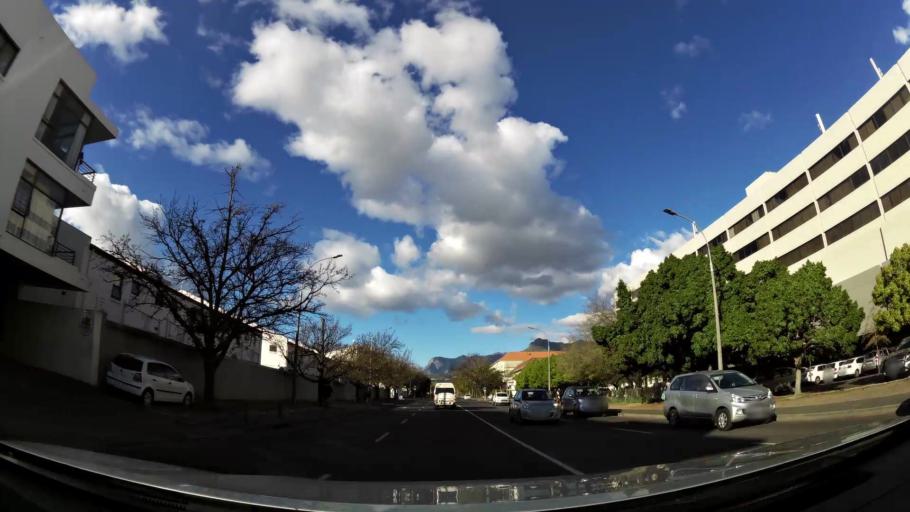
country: ZA
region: Western Cape
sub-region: Cape Winelands District Municipality
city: Stellenbosch
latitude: -33.9320
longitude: 18.8611
